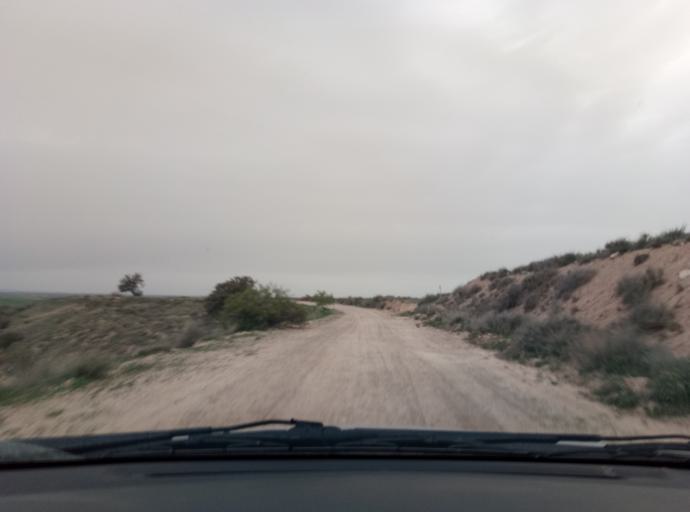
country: ES
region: Catalonia
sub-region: Provincia de Lleida
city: Verdu
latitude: 41.6125
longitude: 1.1062
